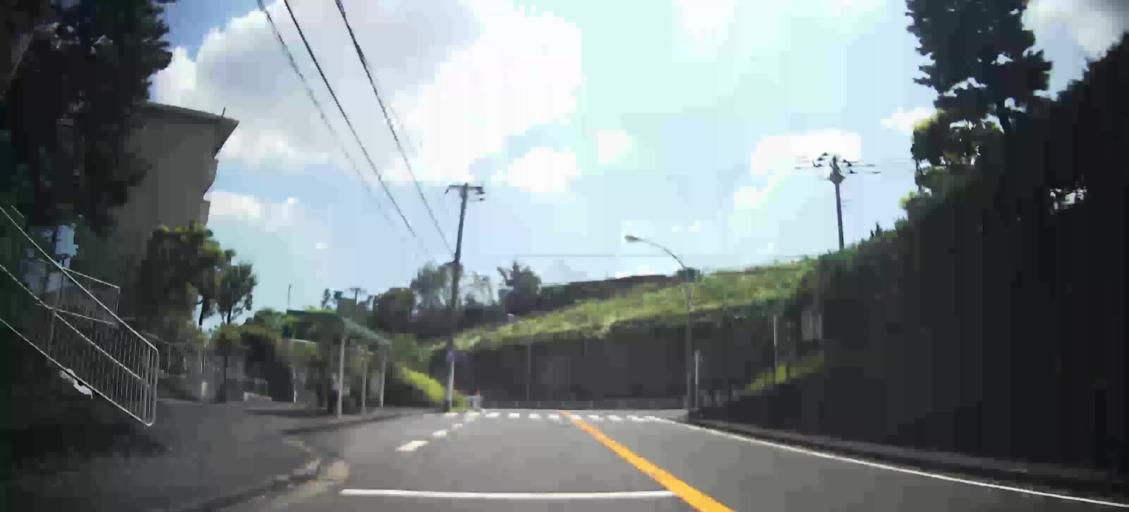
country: JP
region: Kanagawa
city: Yokohama
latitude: 35.4548
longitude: 139.5561
